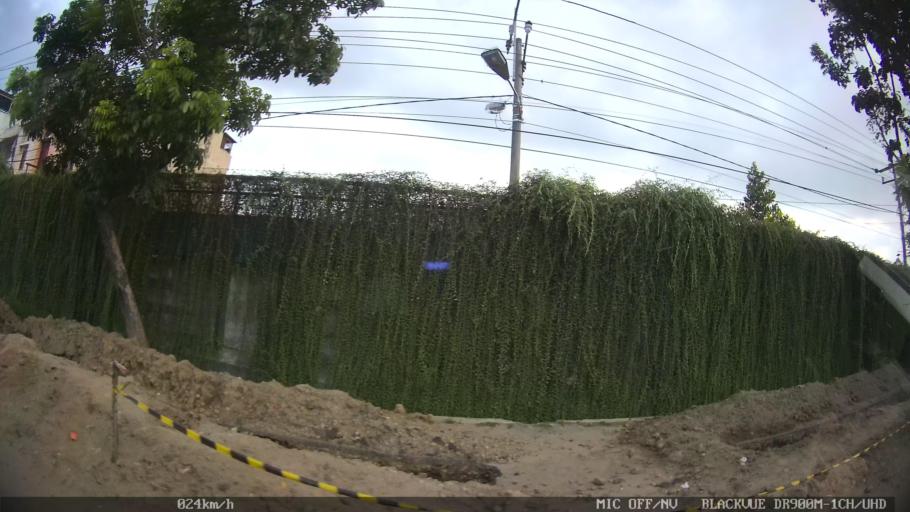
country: ID
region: North Sumatra
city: Medan
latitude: 3.5968
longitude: 98.7432
